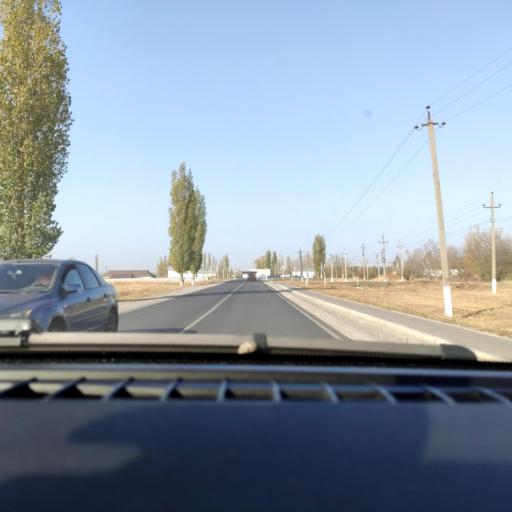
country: RU
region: Voronezj
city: Novaya Usman'
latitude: 51.6583
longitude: 39.4036
